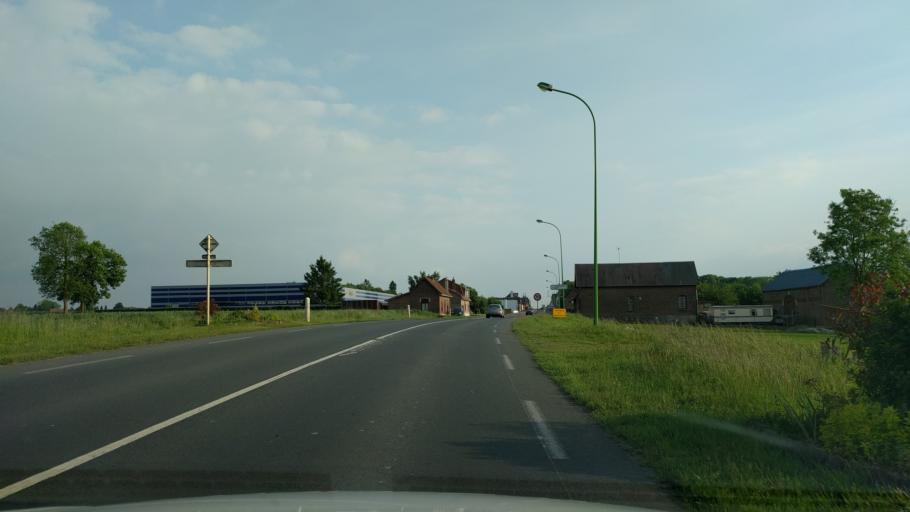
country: FR
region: Picardie
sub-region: Departement de la Somme
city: Moislains
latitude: 50.0357
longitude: 2.9141
